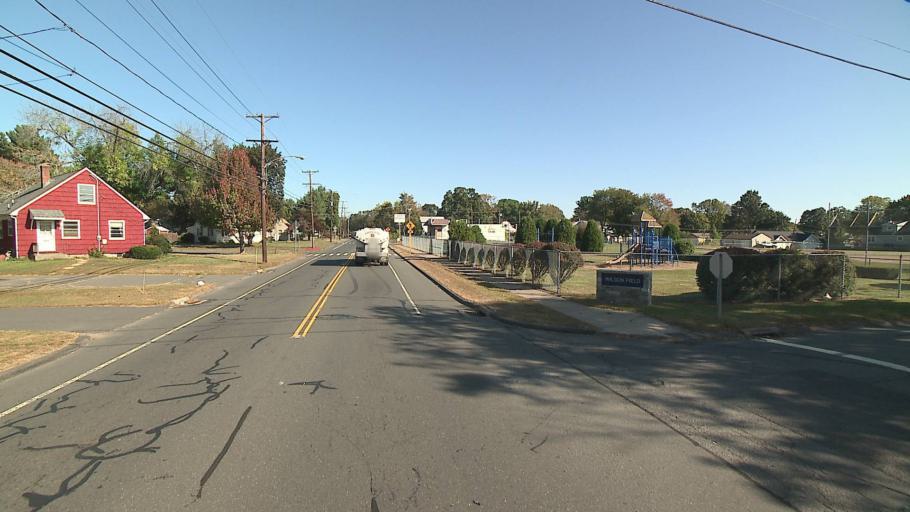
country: US
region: Connecticut
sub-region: Hartford County
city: Bristol
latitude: 41.6742
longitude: -72.9204
